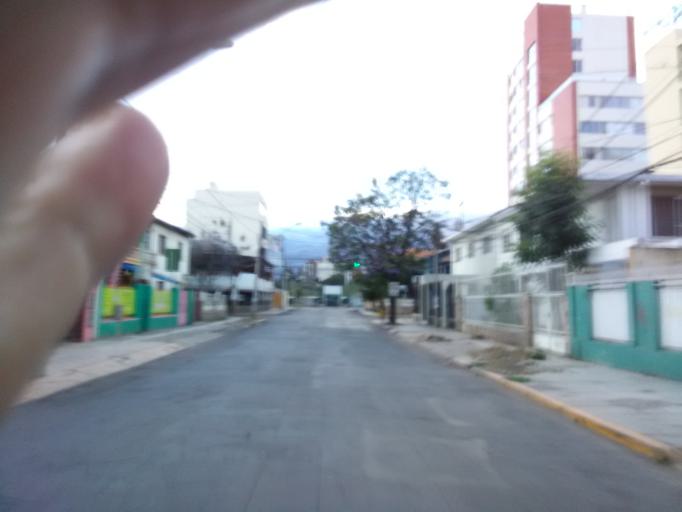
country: BO
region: Cochabamba
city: Cochabamba
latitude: -17.3827
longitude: -66.1562
